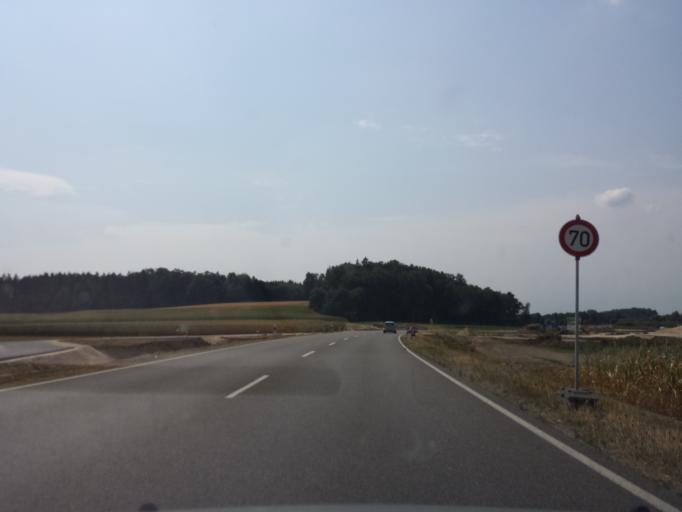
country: DE
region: Bavaria
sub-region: Swabia
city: Nersingen
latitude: 48.4178
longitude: 10.1041
